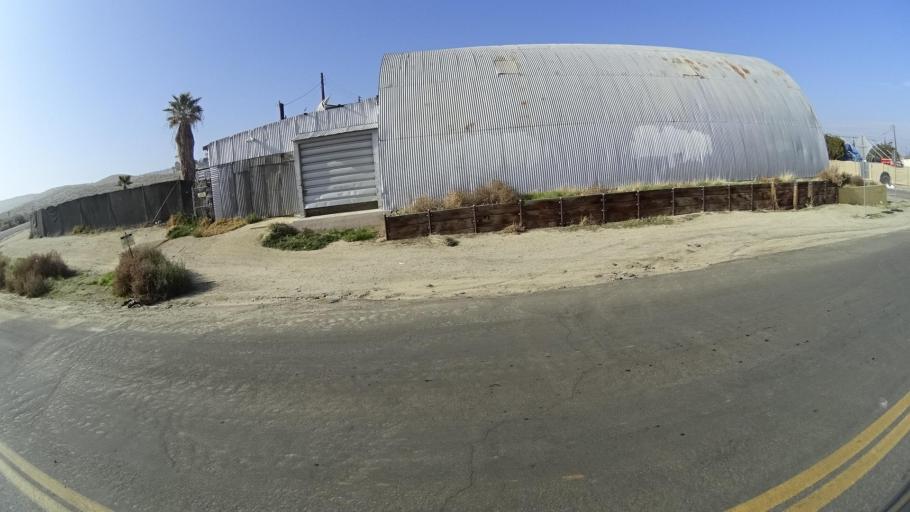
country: US
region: California
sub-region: Kern County
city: Taft Heights
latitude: 35.1324
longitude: -119.4647
